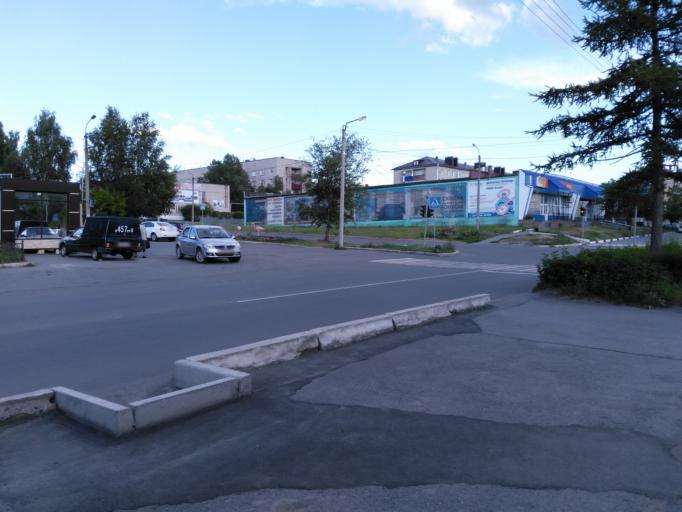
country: RU
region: Bashkortostan
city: Uchaly
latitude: 54.3176
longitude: 59.3835
